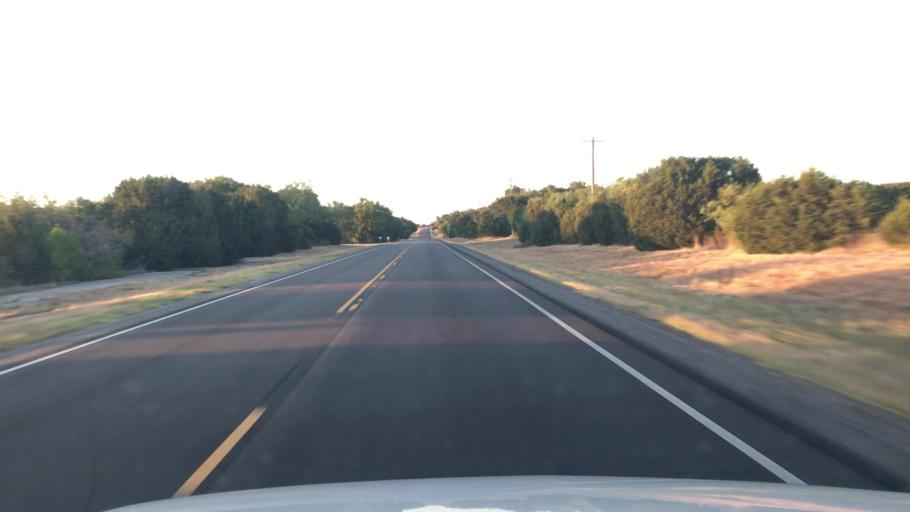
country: US
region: Texas
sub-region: Hamilton County
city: Hico
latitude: 32.0507
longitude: -98.0009
